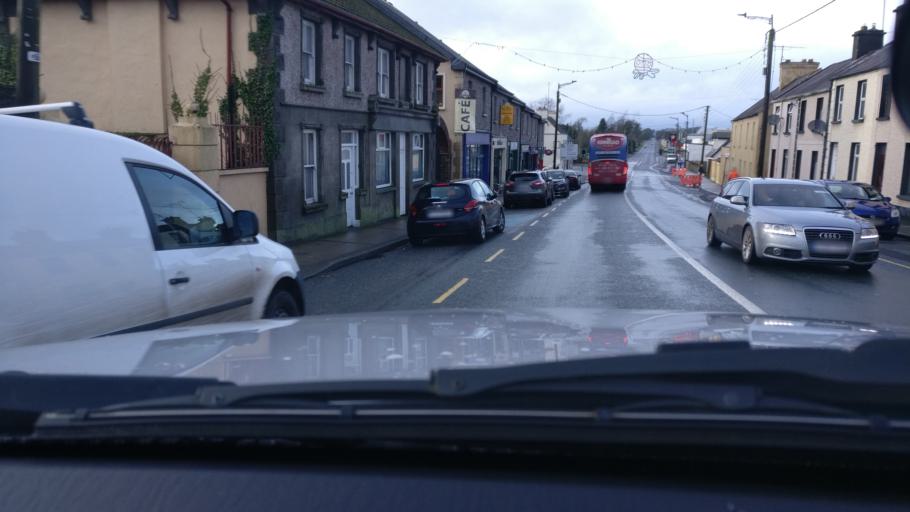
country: IE
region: Leinster
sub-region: An Longfort
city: Edgeworthstown
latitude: 53.6966
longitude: -7.6101
